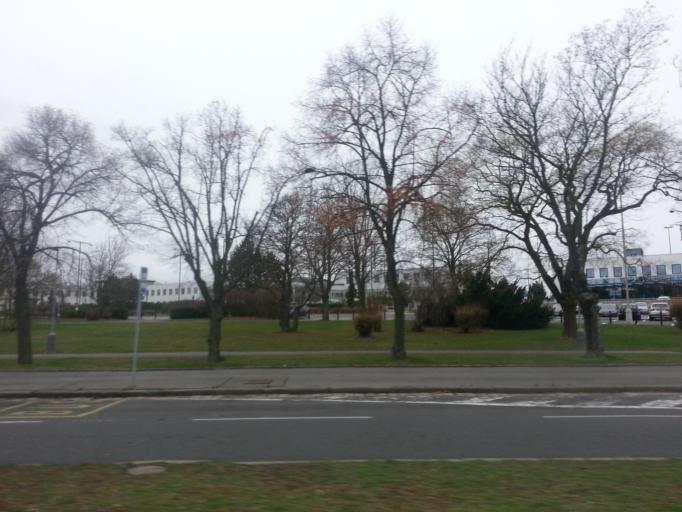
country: CZ
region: Central Bohemia
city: Hostivice
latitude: 50.0994
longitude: 14.2883
